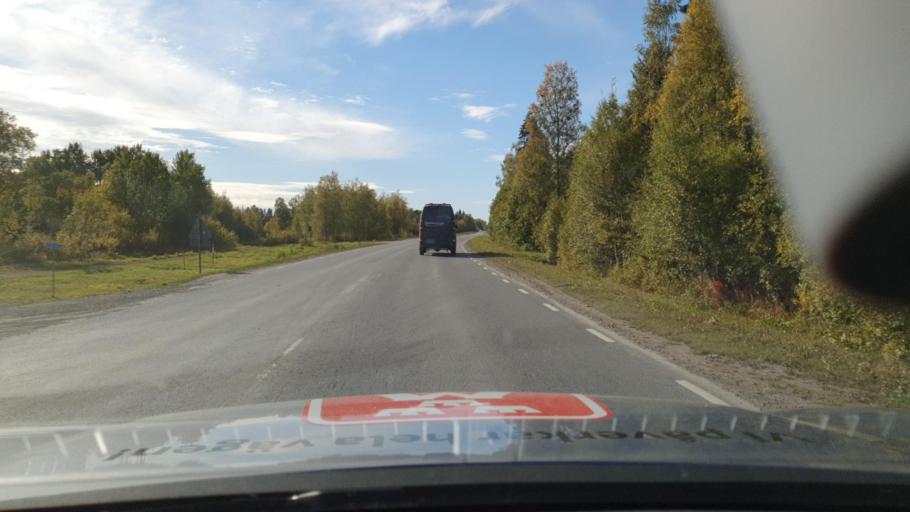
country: SE
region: Norrbotten
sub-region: Haparanda Kommun
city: Haparanda
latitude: 65.8258
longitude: 24.0952
